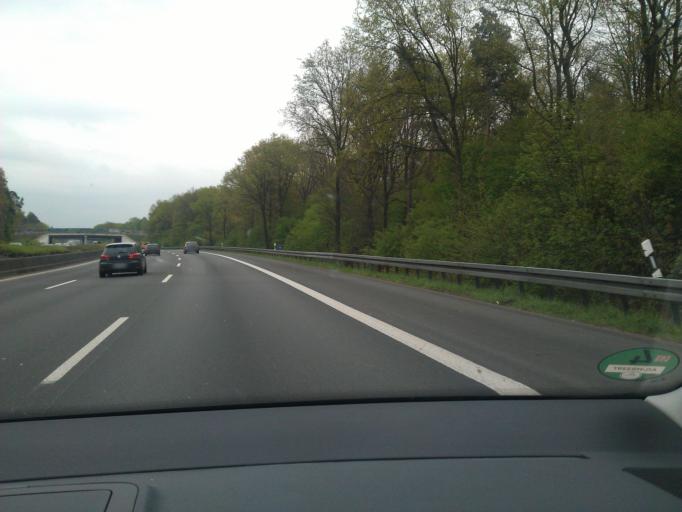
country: DE
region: North Rhine-Westphalia
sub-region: Regierungsbezirk Koln
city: Rath
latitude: 50.9084
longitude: 7.1160
